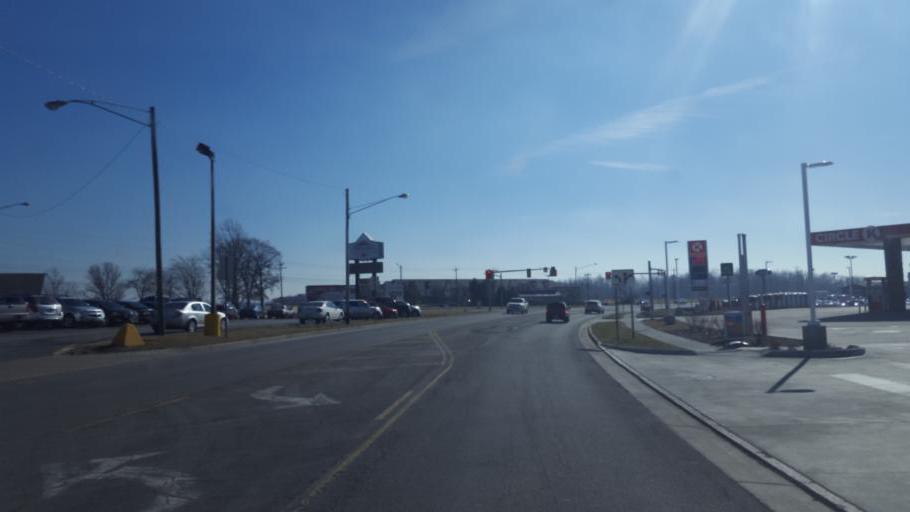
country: US
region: Ohio
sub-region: Huron County
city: Willard
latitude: 41.0419
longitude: -82.7172
